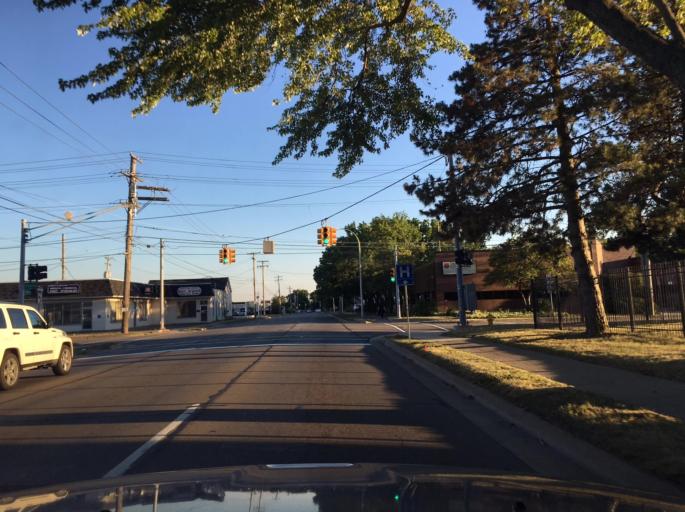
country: US
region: Michigan
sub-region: Macomb County
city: Mount Clemens
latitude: 42.5941
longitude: -82.8808
